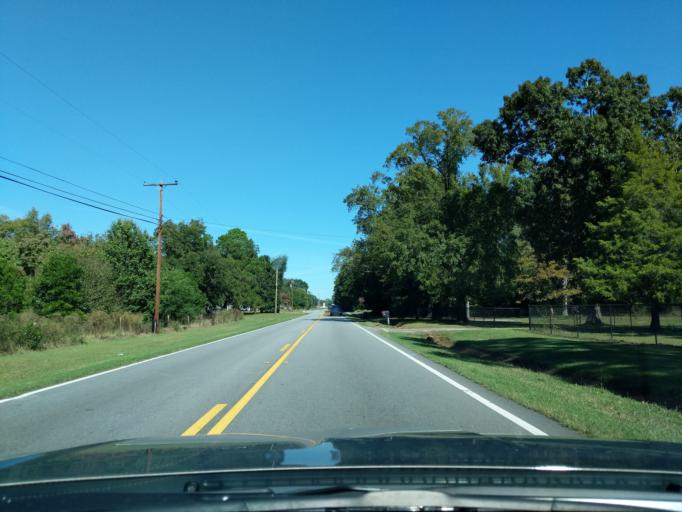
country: US
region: Georgia
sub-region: Richmond County
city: Hephzibah
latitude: 33.3613
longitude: -81.9971
